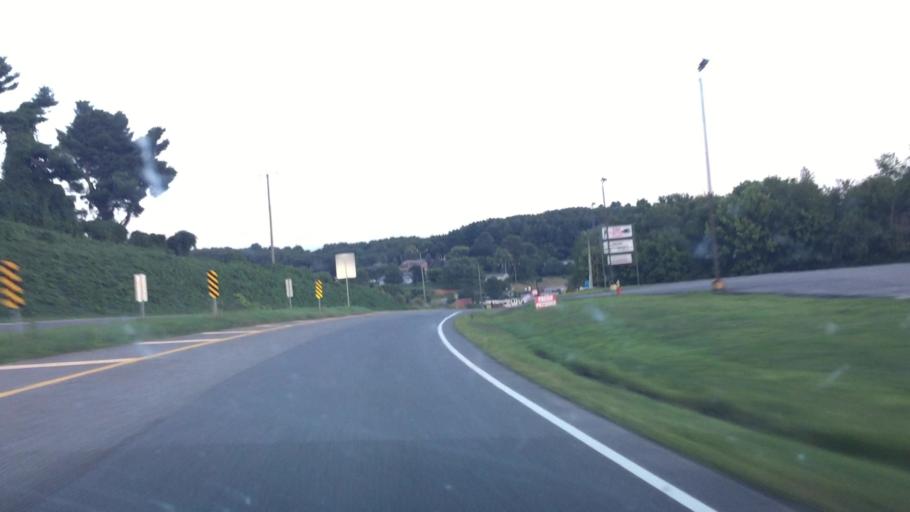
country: US
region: Virginia
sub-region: Wythe County
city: Wytheville
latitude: 36.9426
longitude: -80.9450
